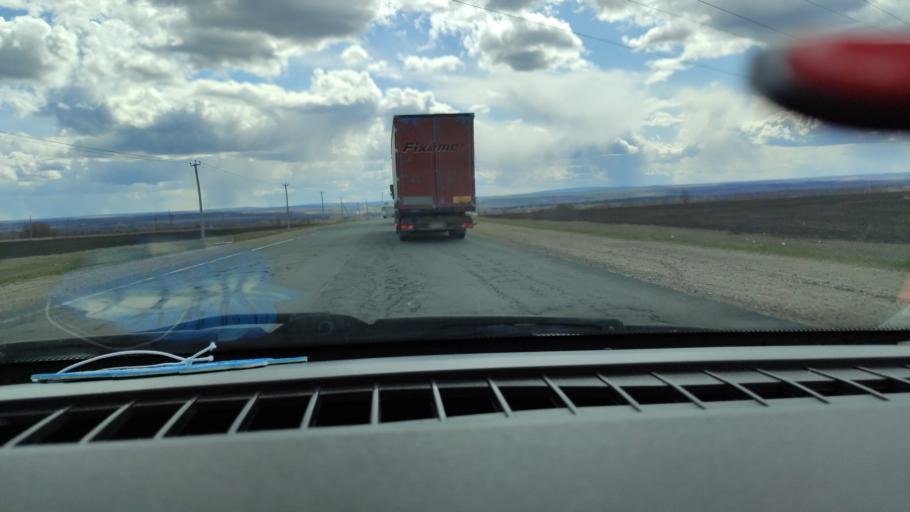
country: RU
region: Samara
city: Varlamovo
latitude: 53.1827
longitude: 48.2884
